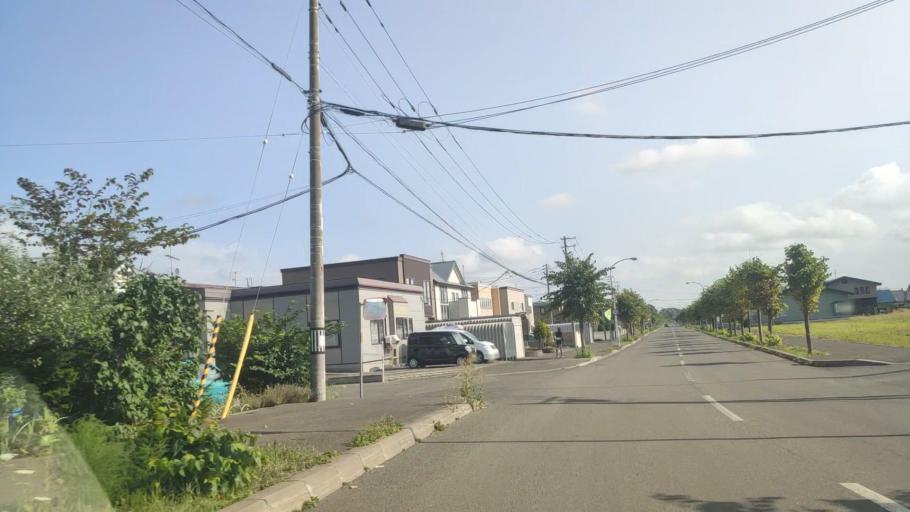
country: JP
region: Hokkaido
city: Shimo-furano
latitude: 43.3481
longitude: 142.3764
